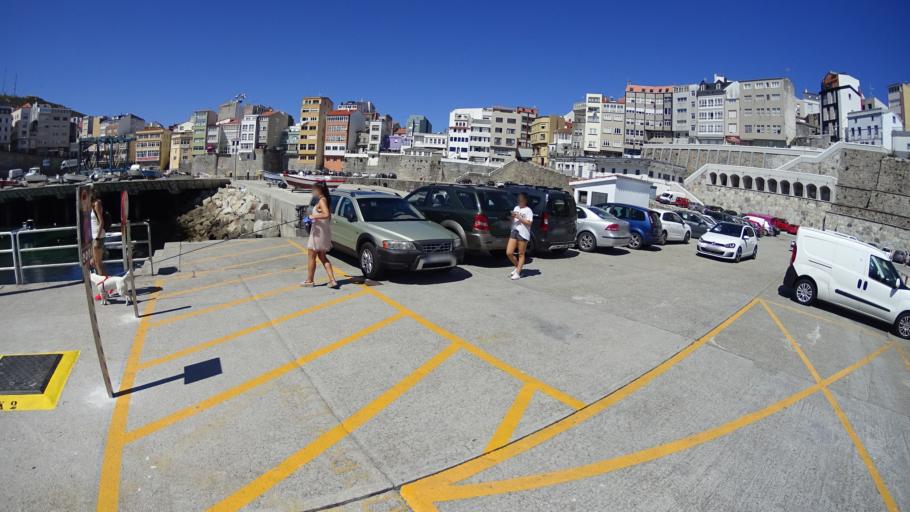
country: ES
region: Galicia
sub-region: Provincia da Coruna
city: Malpica
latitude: 43.3233
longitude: -8.8082
